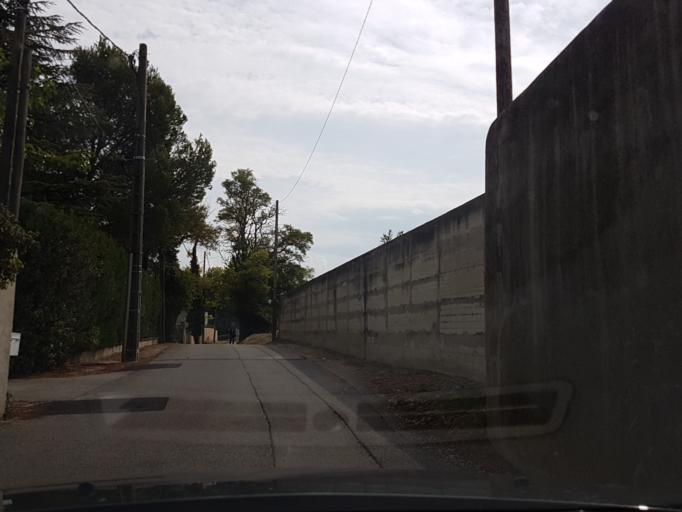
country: FR
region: Provence-Alpes-Cote d'Azur
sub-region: Departement du Vaucluse
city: Jonquerettes
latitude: 43.9533
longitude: 4.9327
